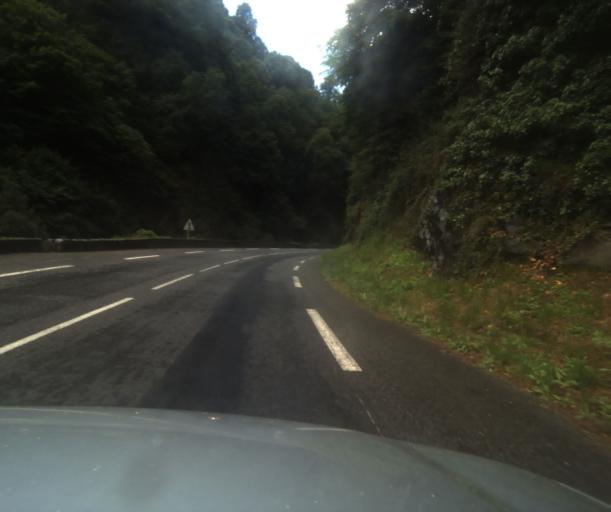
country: FR
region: Midi-Pyrenees
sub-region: Departement des Hautes-Pyrenees
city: Pierrefitte-Nestalas
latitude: 42.9370
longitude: -0.0489
